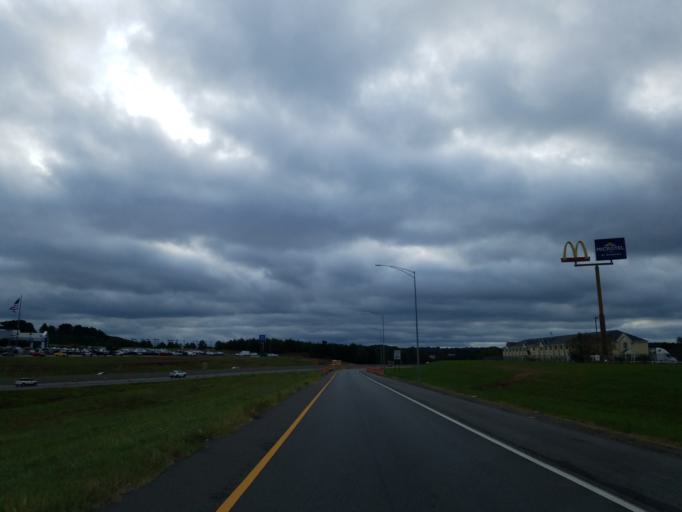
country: US
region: Alabama
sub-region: Tuscaloosa County
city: Holt
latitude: 33.1738
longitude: -87.4487
